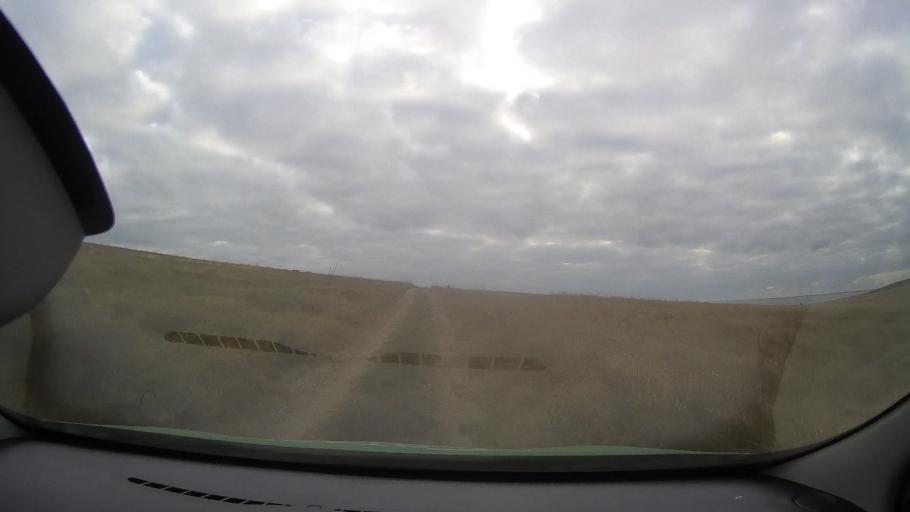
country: RO
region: Tulcea
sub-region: Comuna Jurilovca
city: Jurilovca
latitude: 44.7652
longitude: 28.9243
